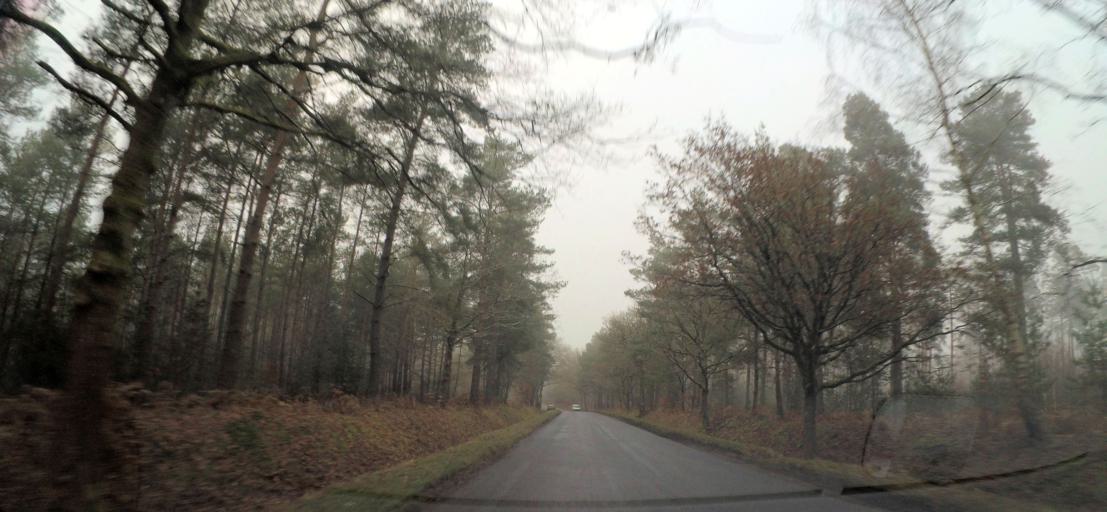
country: GB
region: England
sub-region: West Berkshire
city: Theale
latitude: 51.3880
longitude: -1.0882
